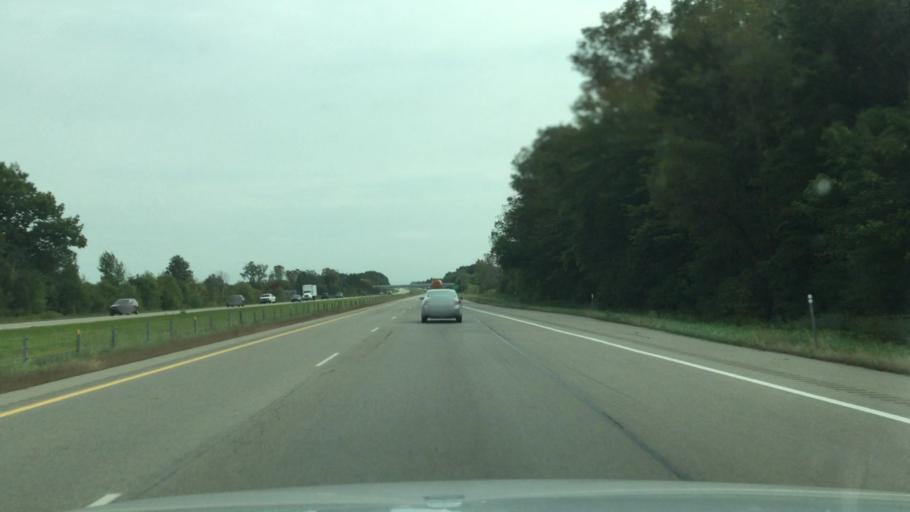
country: US
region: Michigan
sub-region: Genesee County
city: Swartz Creek
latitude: 42.9646
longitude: -83.8597
